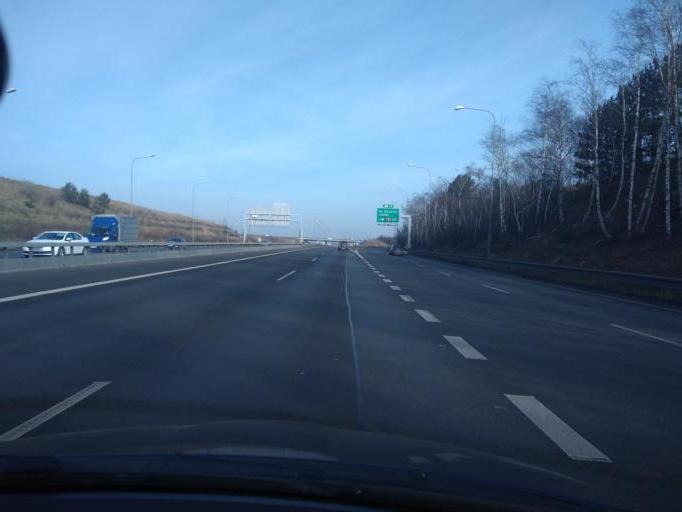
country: CZ
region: Praha
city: Cerny Most
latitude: 50.1139
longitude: 14.5882
